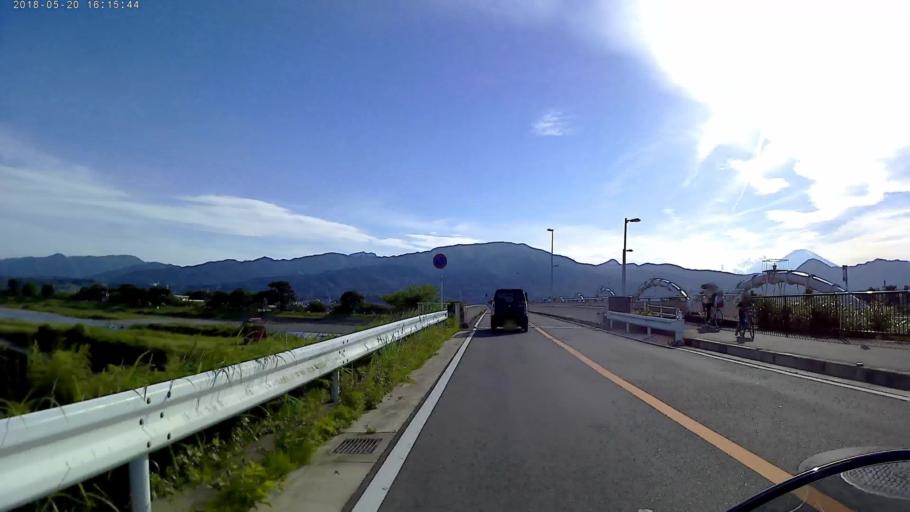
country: JP
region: Kanagawa
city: Odawara
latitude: 35.3127
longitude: 139.1509
